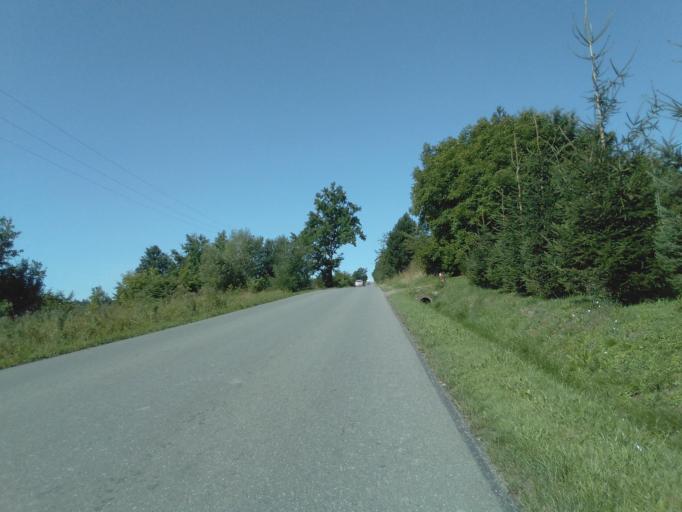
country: PL
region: Subcarpathian Voivodeship
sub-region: Powiat krosnienski
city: Dukla
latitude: 49.5999
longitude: 21.7054
